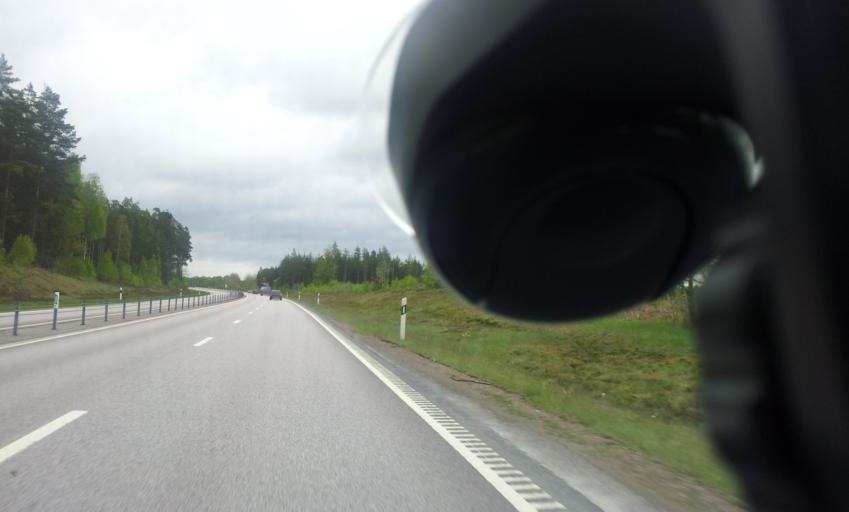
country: SE
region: Kalmar
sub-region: Kalmar Kommun
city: Ljungbyholm
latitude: 56.6295
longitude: 16.1967
